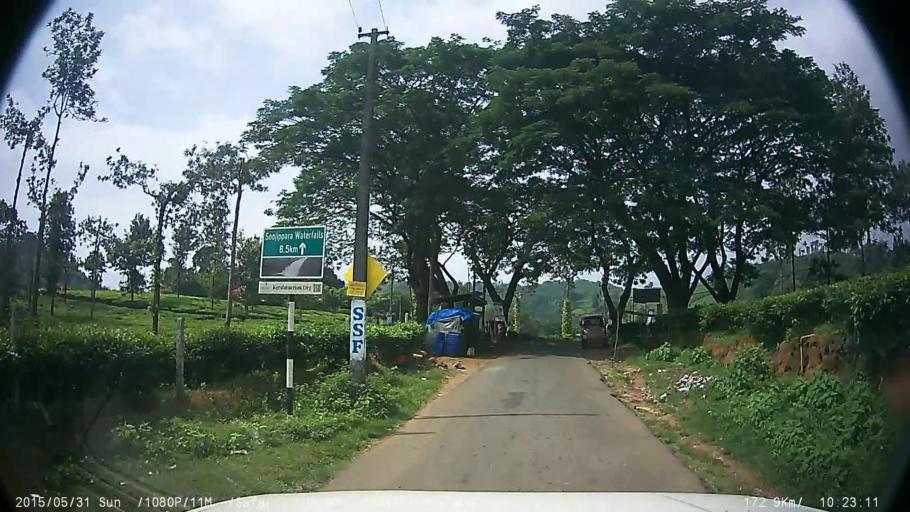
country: IN
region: Kerala
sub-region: Wayanad
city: Kalpetta
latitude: 11.5353
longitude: 76.1350
